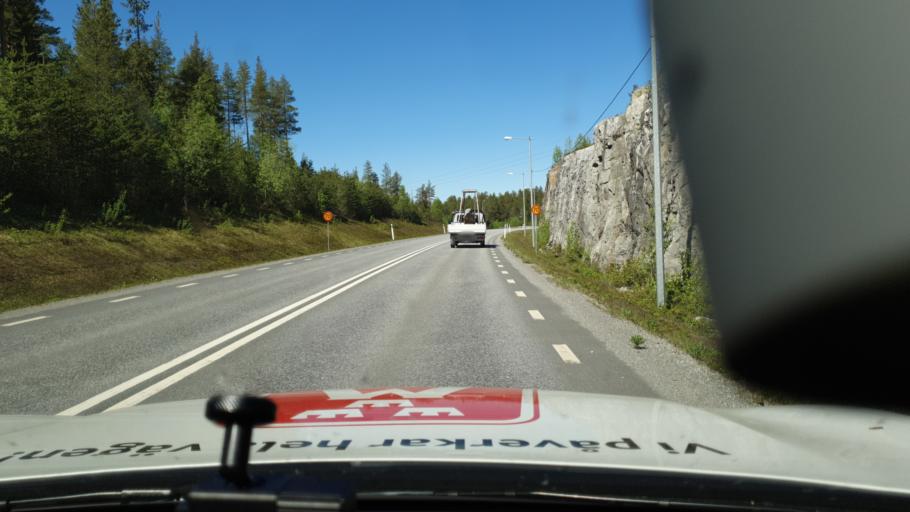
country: SE
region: Vaesterbotten
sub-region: Storumans Kommun
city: Storuman
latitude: 65.0815
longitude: 17.1126
